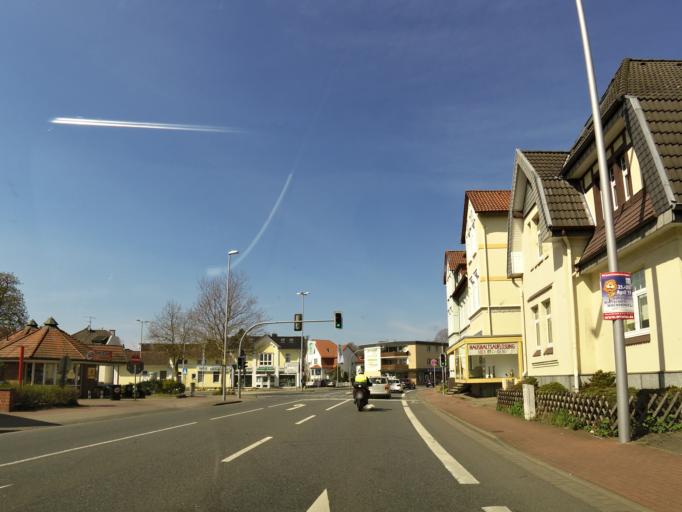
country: DE
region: Lower Saxony
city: Wunstorf
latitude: 52.4223
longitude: 9.4326
